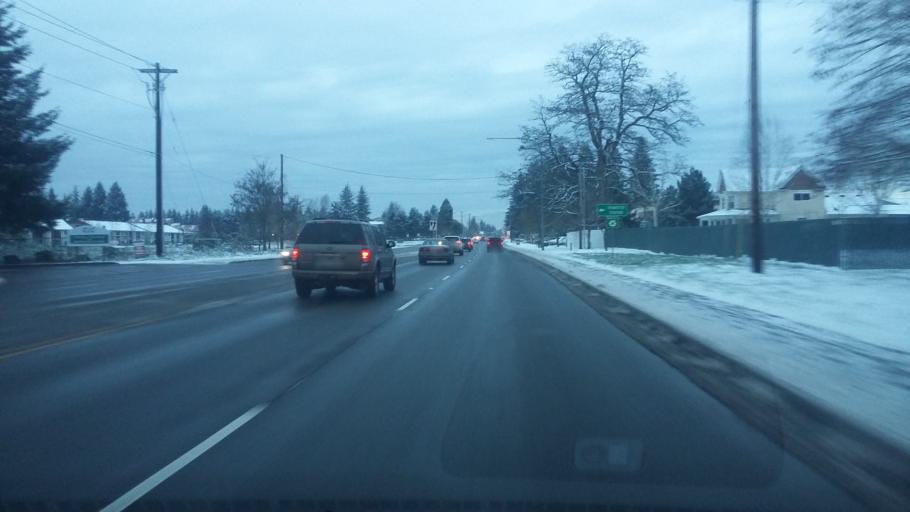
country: US
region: Washington
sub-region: Clark County
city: Five Corners
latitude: 45.7012
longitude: -122.5527
